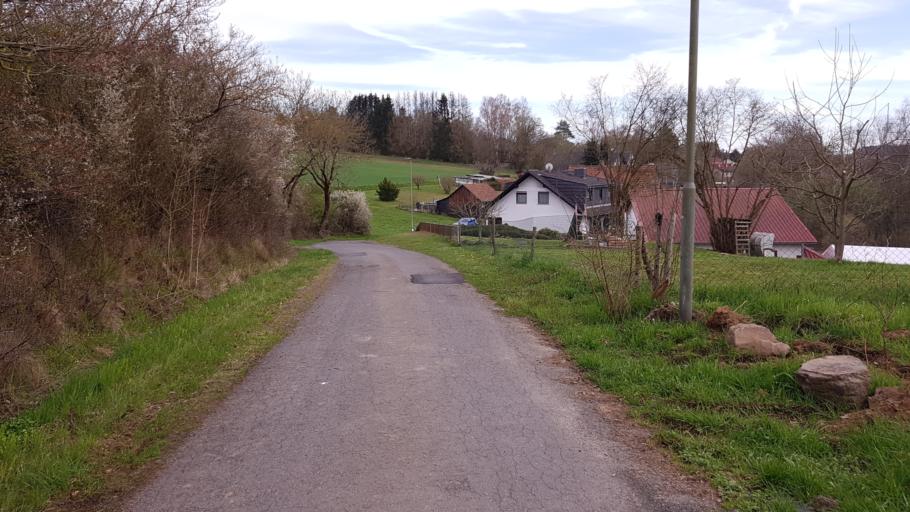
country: DE
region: Hesse
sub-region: Regierungsbezirk Giessen
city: Homberg
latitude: 50.6553
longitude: 9.0352
